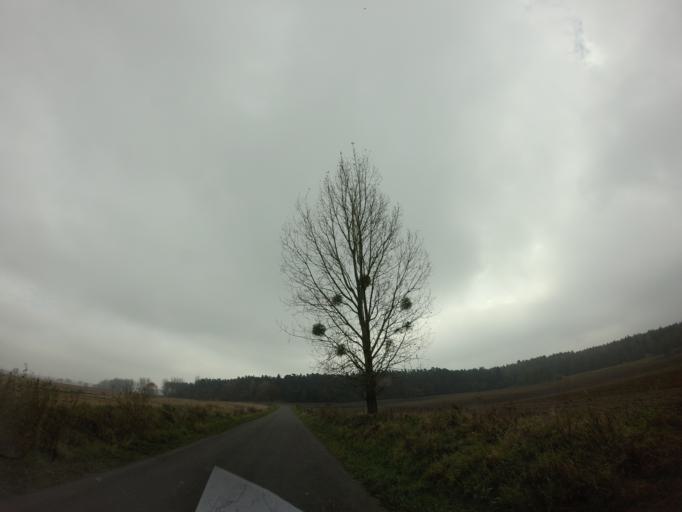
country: PL
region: West Pomeranian Voivodeship
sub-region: Powiat choszczenski
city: Recz
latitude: 53.2015
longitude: 15.5568
